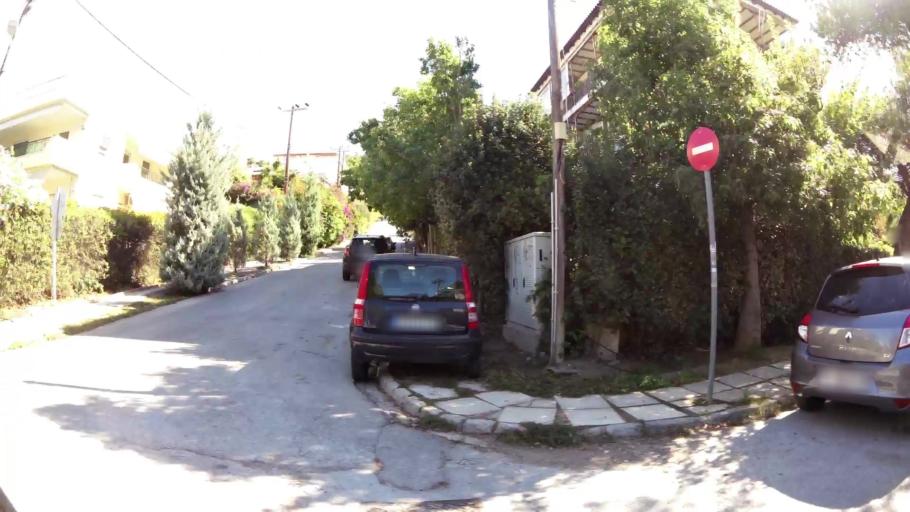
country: GR
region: Attica
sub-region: Nomarchia Anatolikis Attikis
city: Voula
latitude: 37.8291
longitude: 23.7789
